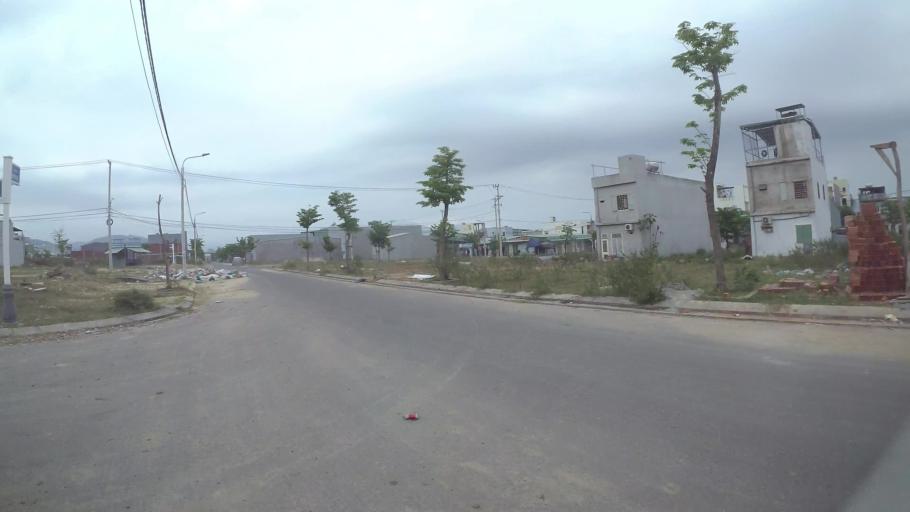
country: VN
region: Da Nang
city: Lien Chieu
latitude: 16.0414
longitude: 108.1691
